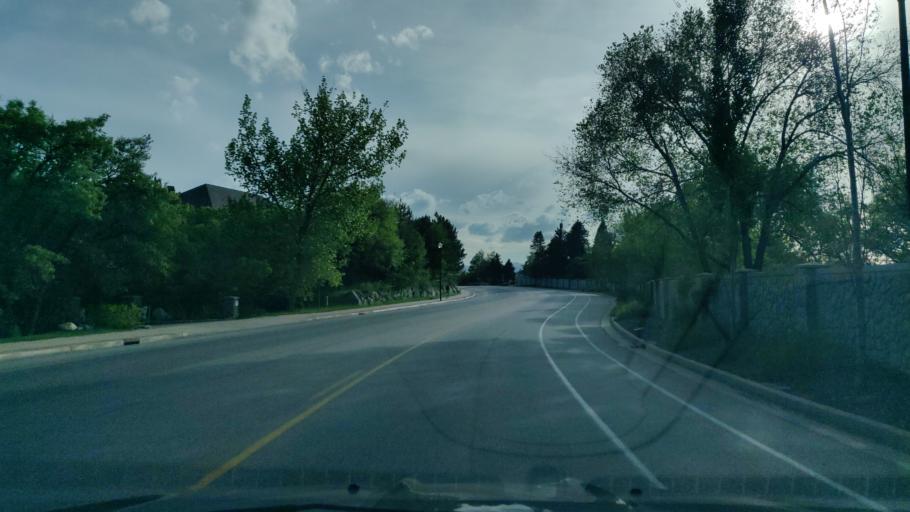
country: US
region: Utah
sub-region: Salt Lake County
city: Granite
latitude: 40.5449
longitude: -111.8081
